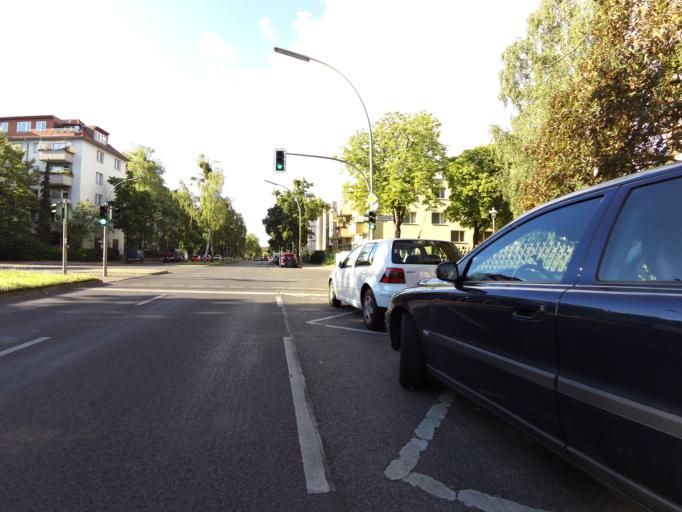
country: DE
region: Berlin
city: Steglitz Bezirk
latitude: 52.4556
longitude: 13.3327
